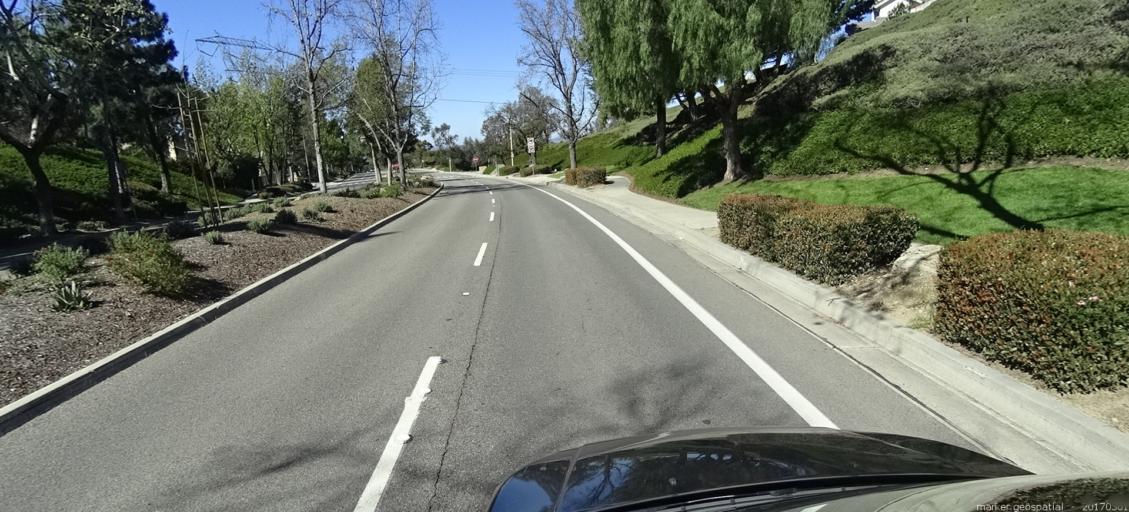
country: US
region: California
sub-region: Orange County
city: Villa Park
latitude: 33.8472
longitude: -117.7563
